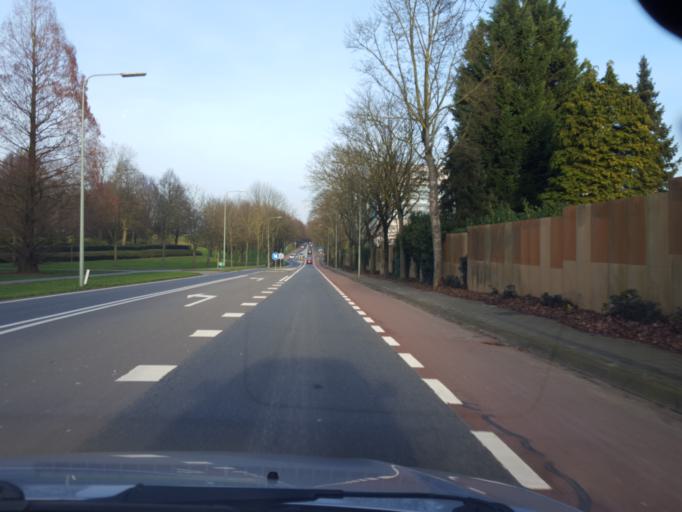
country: NL
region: Limburg
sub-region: Gemeente Heerlen
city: Hoensbroek
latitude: 50.9274
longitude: 5.9161
